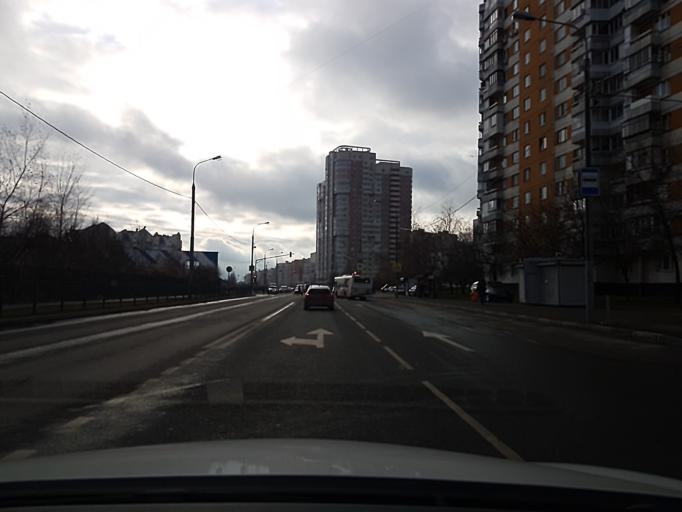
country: RU
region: Moskovskaya
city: Pavshino
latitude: 55.8332
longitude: 37.3566
